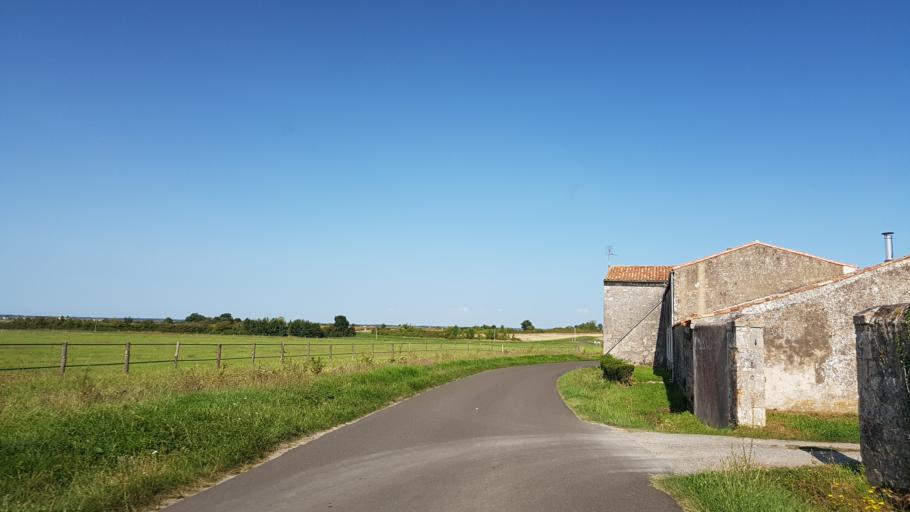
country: FR
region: Poitou-Charentes
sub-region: Departement de la Charente-Maritime
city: Breuillet
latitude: 45.7060
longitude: -1.0438
